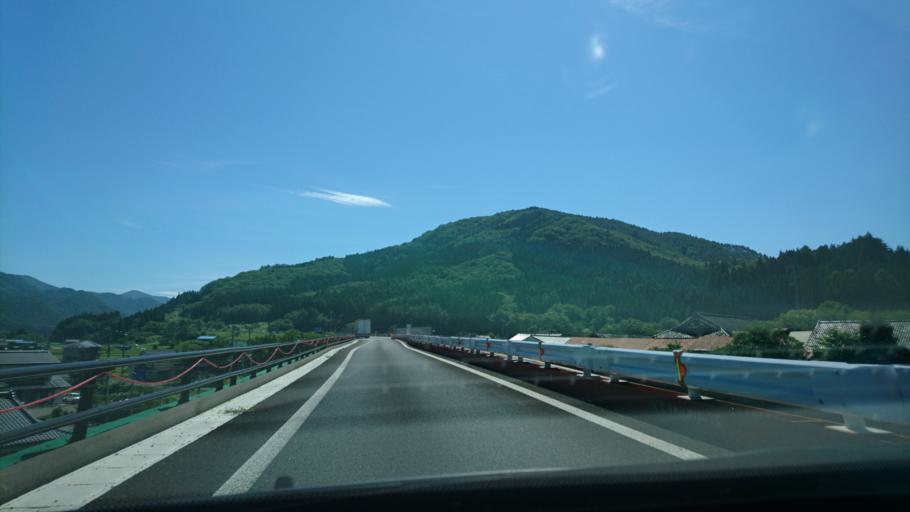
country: JP
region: Iwate
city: Tono
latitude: 39.2636
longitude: 141.5917
